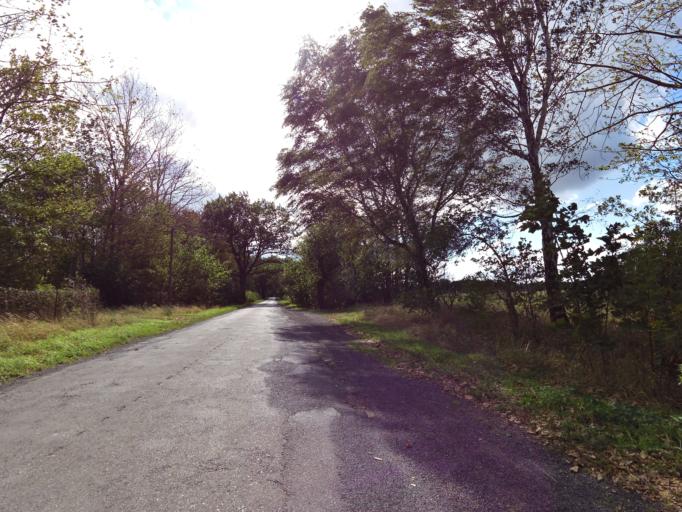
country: DE
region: Brandenburg
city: Grossbeeren
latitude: 52.3657
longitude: 13.3344
